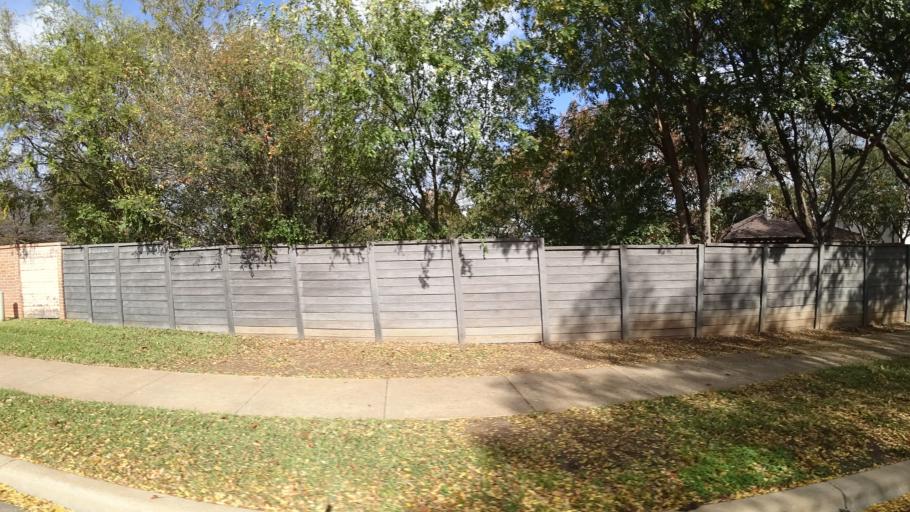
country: US
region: Texas
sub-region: Williamson County
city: Brushy Creek
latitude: 30.5050
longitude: -97.7358
